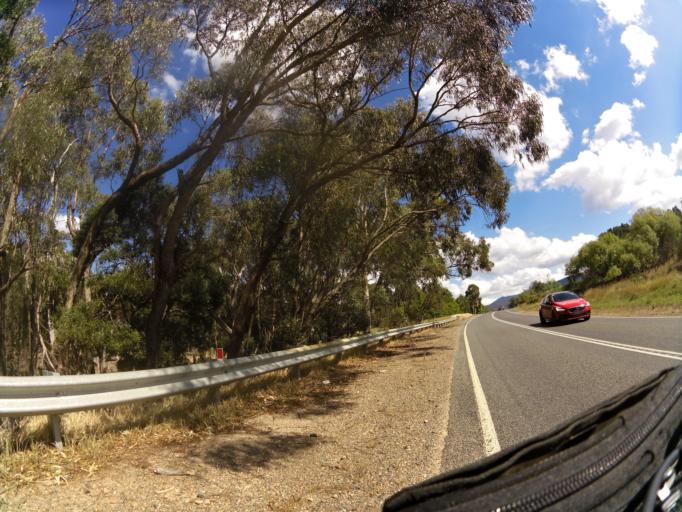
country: AU
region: Victoria
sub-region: Mansfield
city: Mansfield
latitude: -36.8527
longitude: 146.0063
